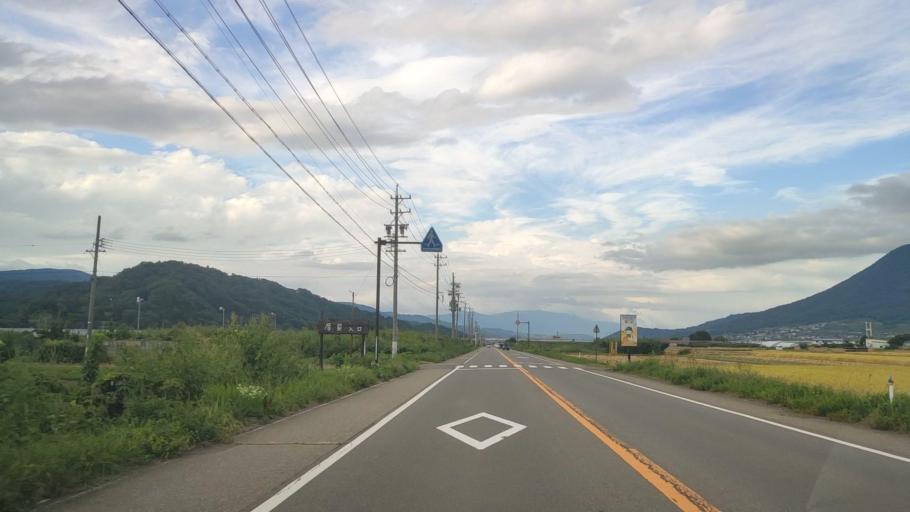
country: JP
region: Nagano
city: Nakano
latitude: 36.7741
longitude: 138.3506
